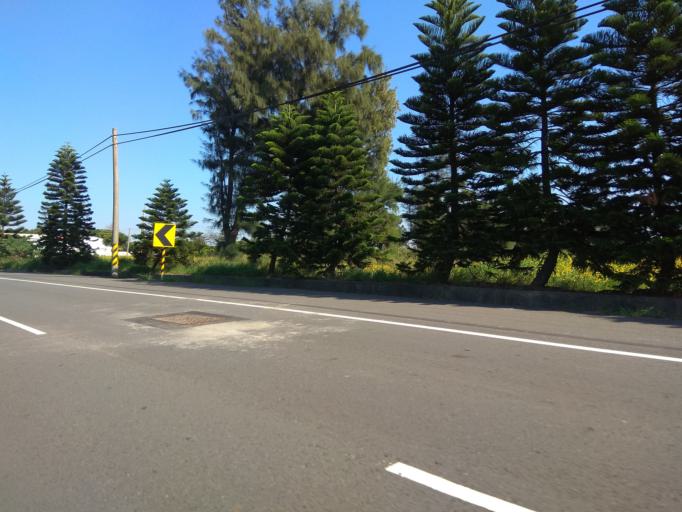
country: TW
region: Taiwan
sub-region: Hsinchu
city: Zhubei
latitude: 25.0206
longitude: 121.0570
